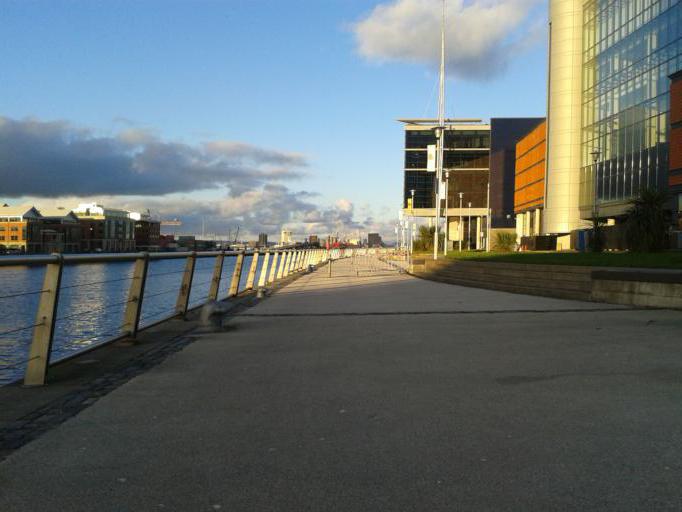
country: GB
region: Northern Ireland
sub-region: City of Belfast
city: Belfast
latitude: 54.6039
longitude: -5.9176
